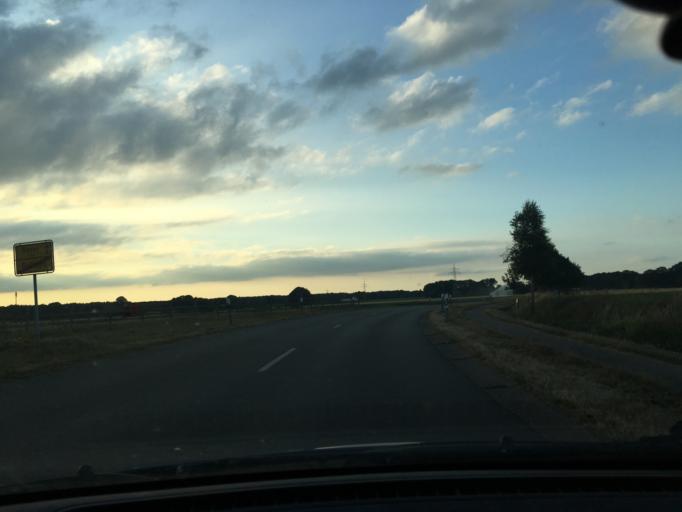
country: DE
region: Lower Saxony
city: Soderstorf
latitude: 53.1653
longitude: 10.1585
